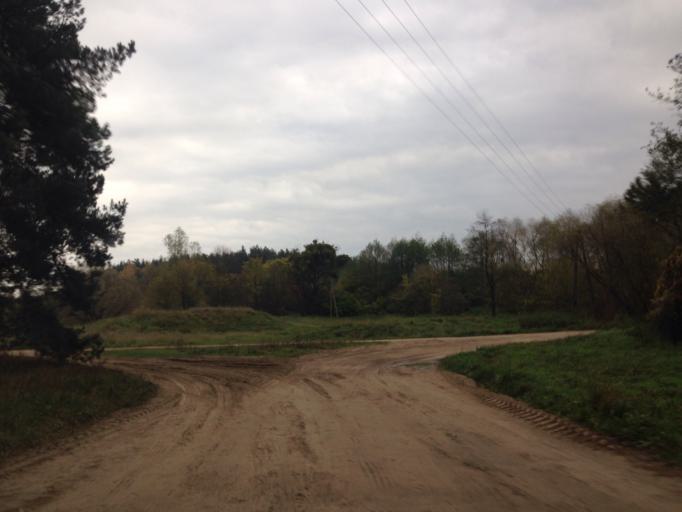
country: PL
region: Kujawsko-Pomorskie
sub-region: Powiat brodnicki
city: Bartniczka
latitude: 53.2867
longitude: 19.5840
